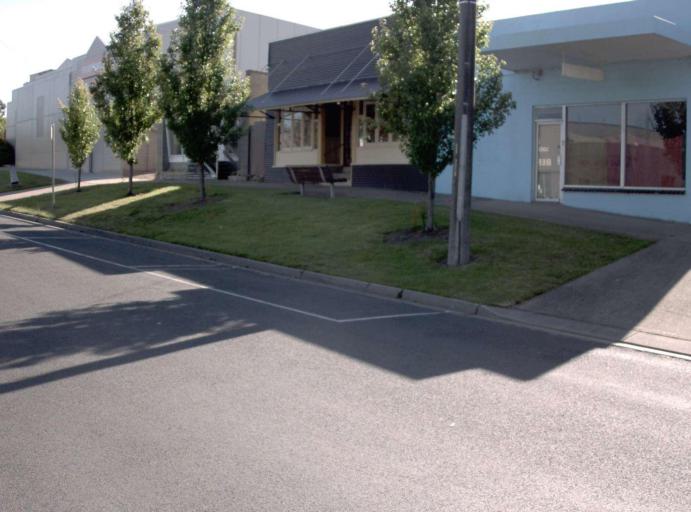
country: AU
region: Victoria
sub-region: East Gippsland
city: Lakes Entrance
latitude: -37.7084
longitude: 148.4543
